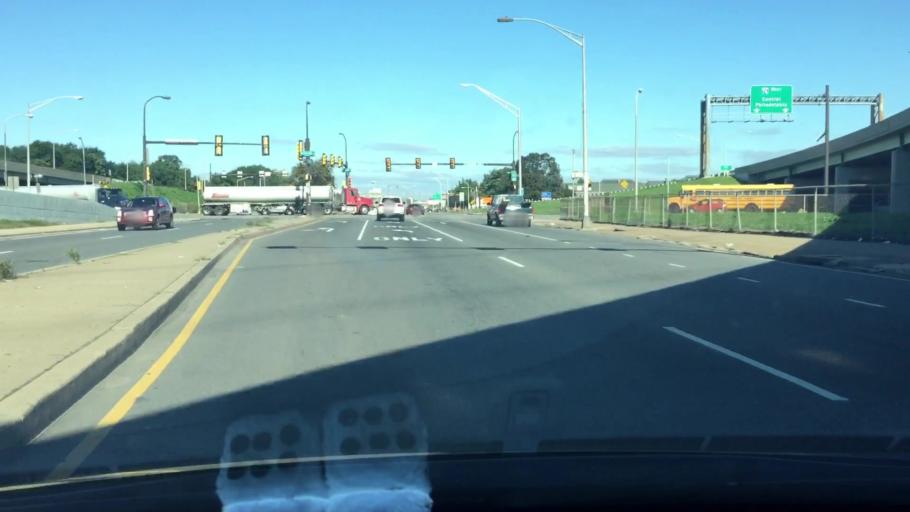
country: US
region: Pennsylvania
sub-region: Philadelphia County
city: Philadelphia
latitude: 39.9208
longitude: -75.1893
